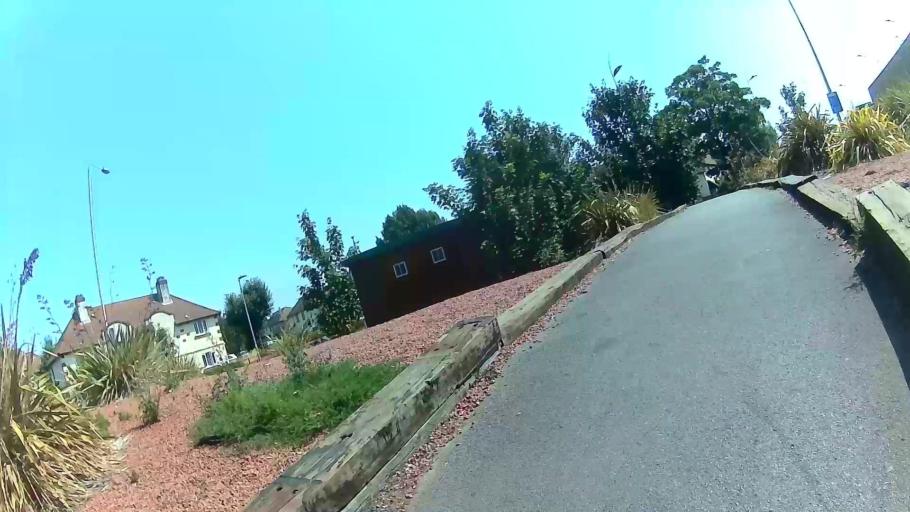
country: GB
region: England
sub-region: Greater London
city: Dagenham
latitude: 51.5319
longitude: 0.1481
